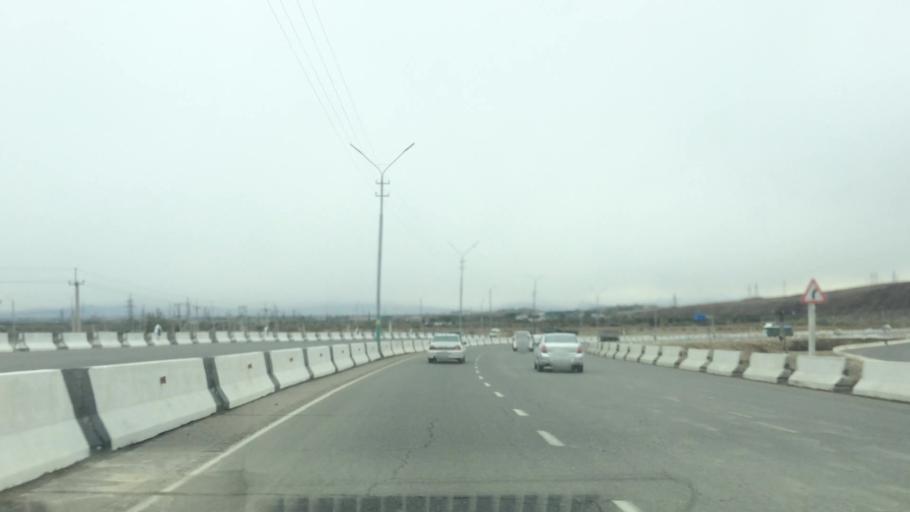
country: UZ
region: Samarqand
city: Jomboy
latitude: 39.6923
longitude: 67.0676
